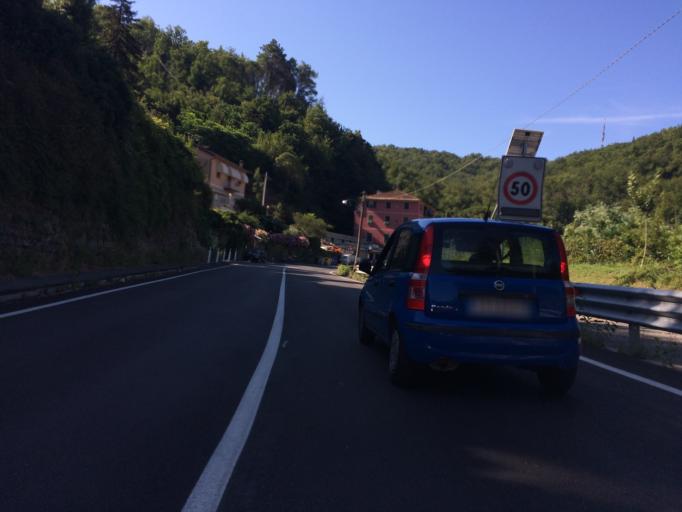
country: IT
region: Liguria
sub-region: Provincia di Genova
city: Camogli
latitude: 44.3428
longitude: 9.1752
